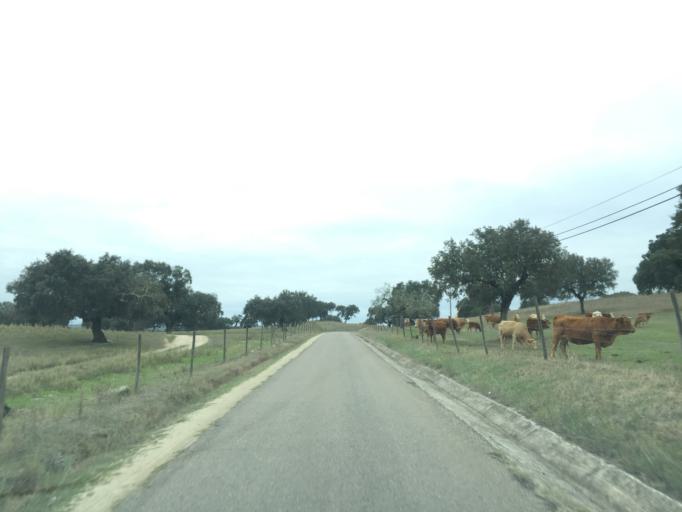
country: PT
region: Portalegre
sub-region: Fronteira
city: Vale da Amoreira
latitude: 39.0501
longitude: -7.7818
